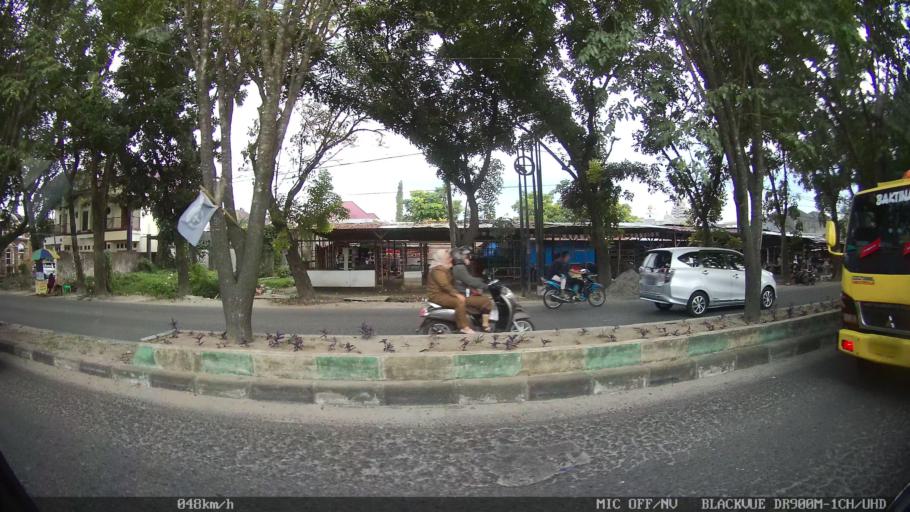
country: ID
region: North Sumatra
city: Sunggal
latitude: 3.5494
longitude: 98.6085
